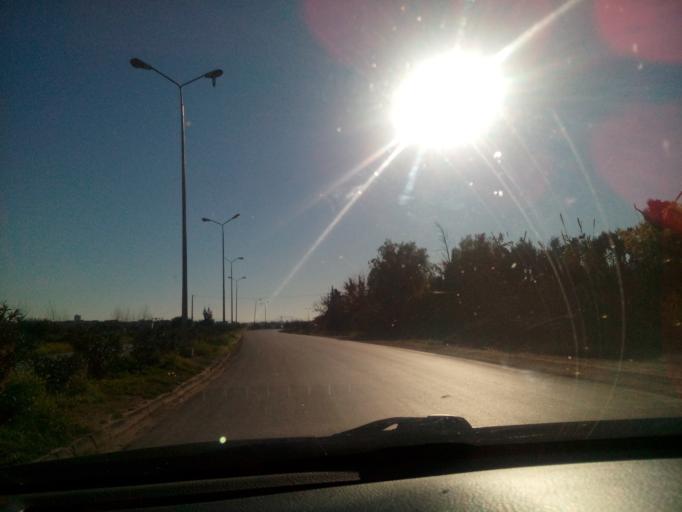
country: DZ
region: Relizane
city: Relizane
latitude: 35.7201
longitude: 0.5761
